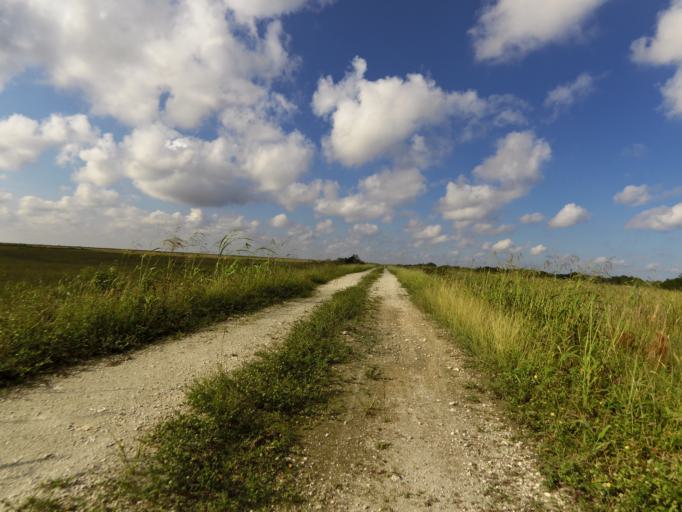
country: US
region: Florida
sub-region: Broward County
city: Weston
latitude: 26.0541
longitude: -80.4630
